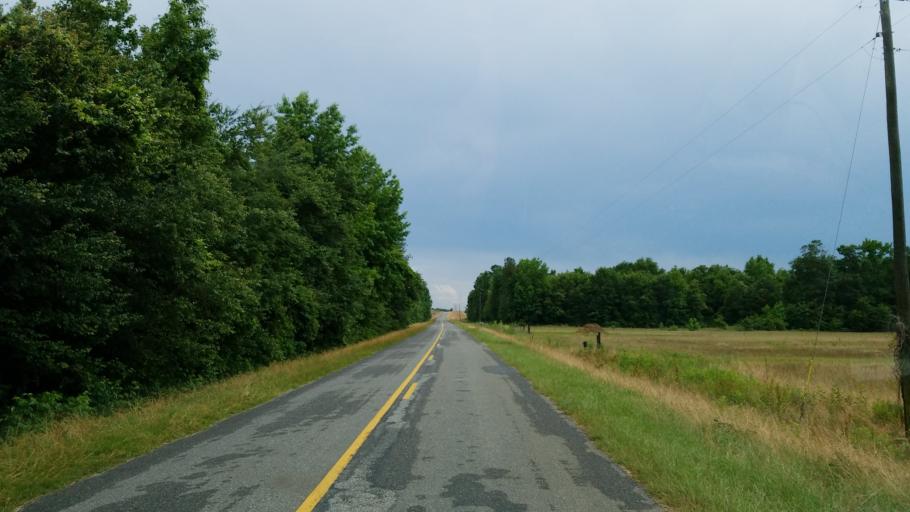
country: US
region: Georgia
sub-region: Dooly County
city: Unadilla
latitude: 32.2684
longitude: -83.7969
